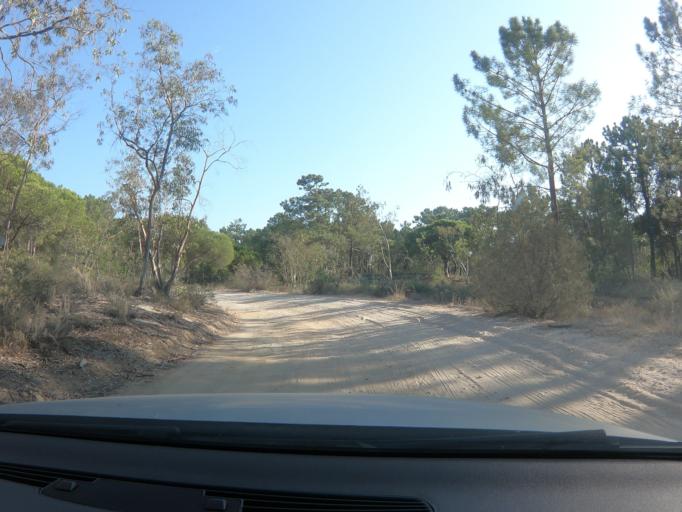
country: PT
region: Setubal
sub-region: Setubal
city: Setubal
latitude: 38.4705
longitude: -8.8774
